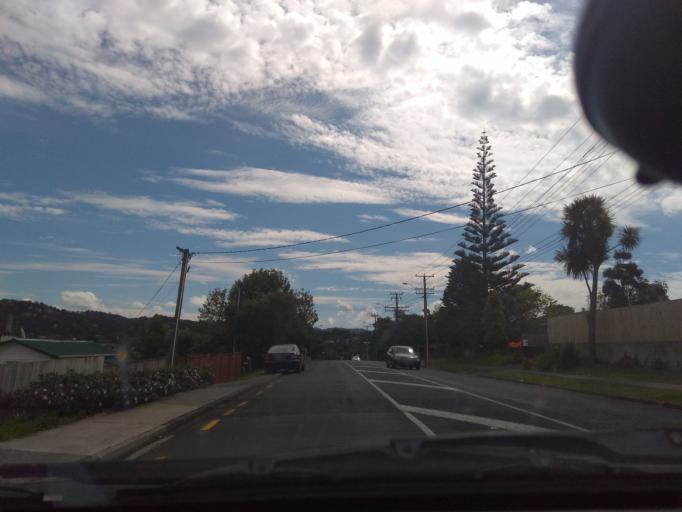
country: NZ
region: Auckland
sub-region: Auckland
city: Waitakere
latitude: -36.9266
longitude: 174.6755
